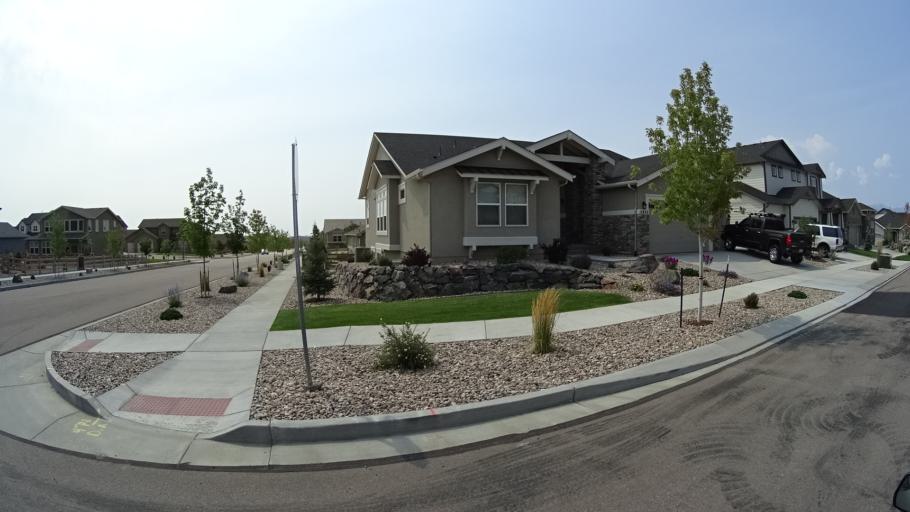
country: US
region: Colorado
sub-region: El Paso County
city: Black Forest
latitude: 38.9699
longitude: -104.7239
